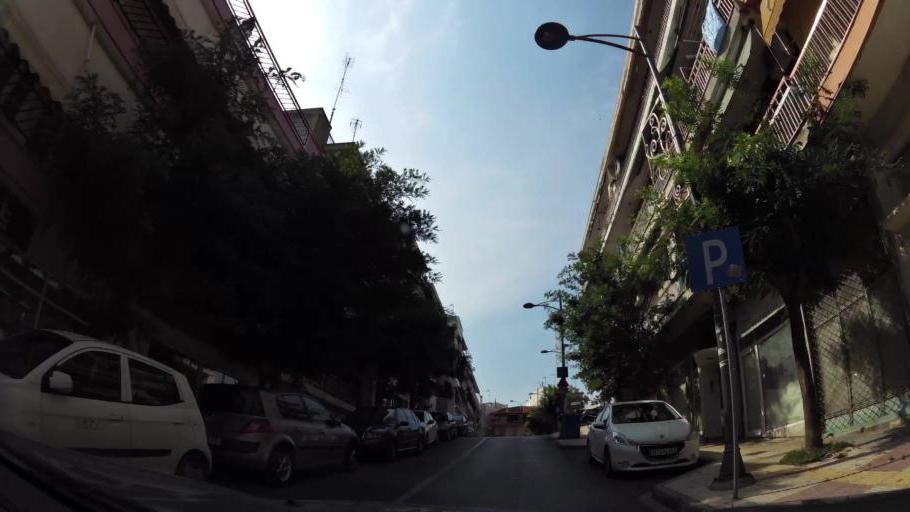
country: GR
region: Central Macedonia
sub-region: Nomos Thessalonikis
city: Sykies
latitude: 40.6475
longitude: 22.9486
